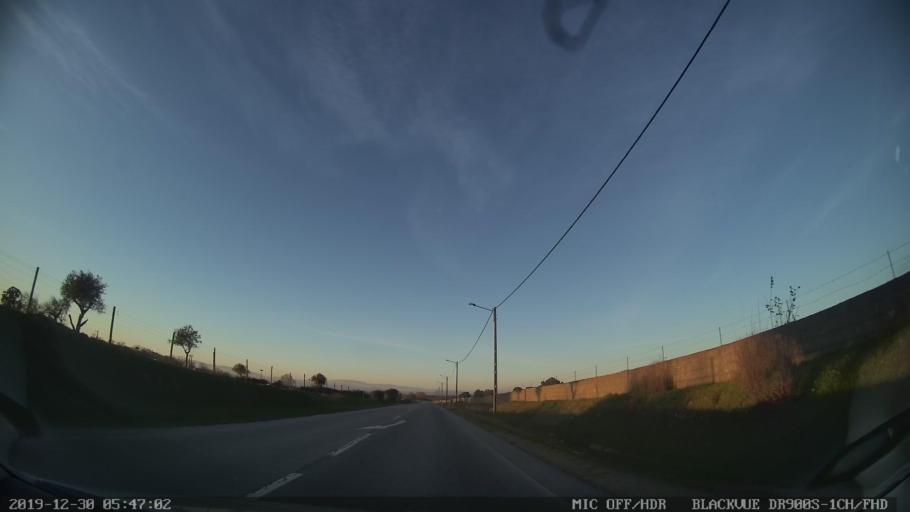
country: PT
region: Castelo Branco
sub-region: Idanha-A-Nova
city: Idanha-a-Nova
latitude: 39.9470
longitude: -7.2375
